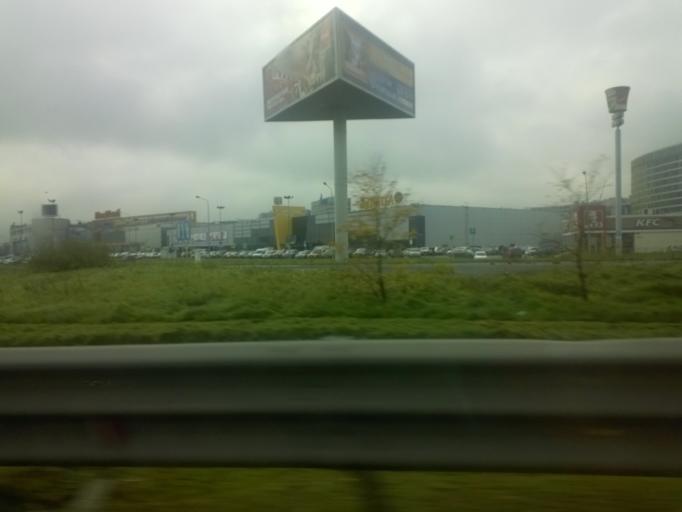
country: RU
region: St.-Petersburg
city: Kupchino
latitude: 59.8094
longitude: 30.3226
